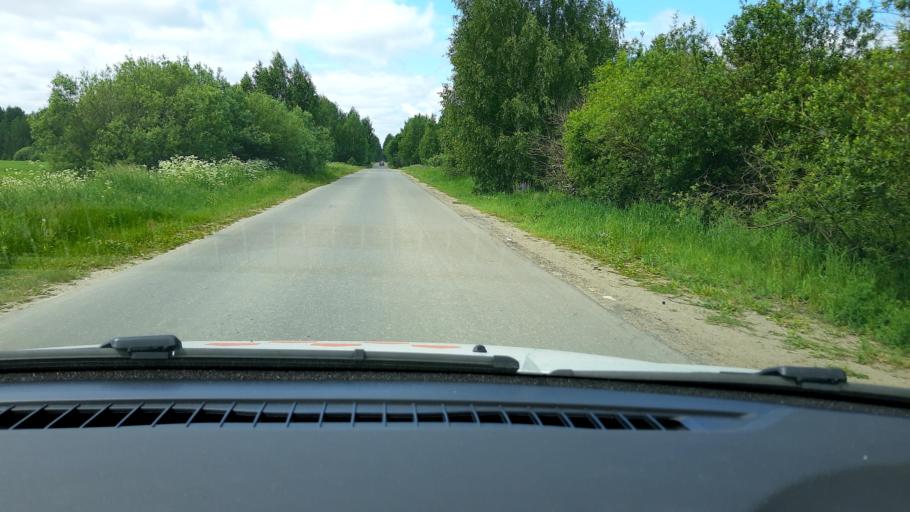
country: RU
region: Nizjnij Novgorod
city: Linda
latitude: 56.5393
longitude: 44.0859
